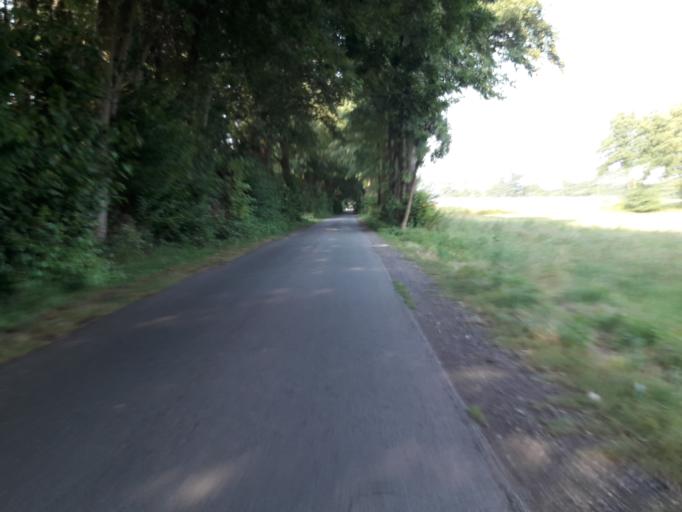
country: DE
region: North Rhine-Westphalia
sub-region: Regierungsbezirk Detmold
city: Hovelhof
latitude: 51.7904
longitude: 8.6662
